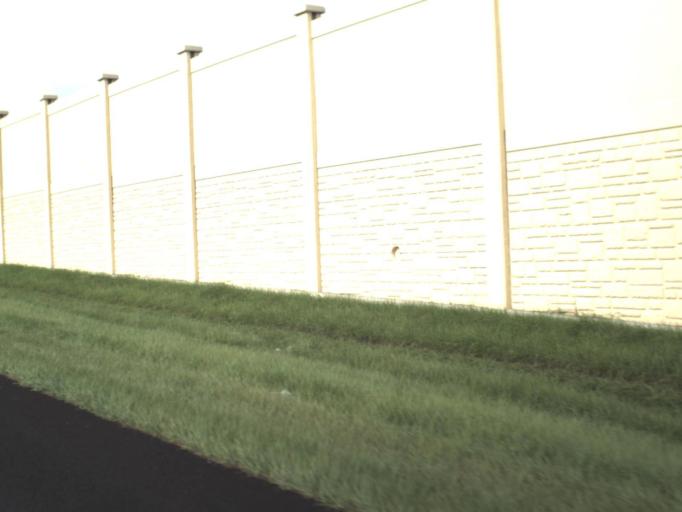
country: US
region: Florida
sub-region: Lake County
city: Four Corners
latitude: 28.2787
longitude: -81.6624
